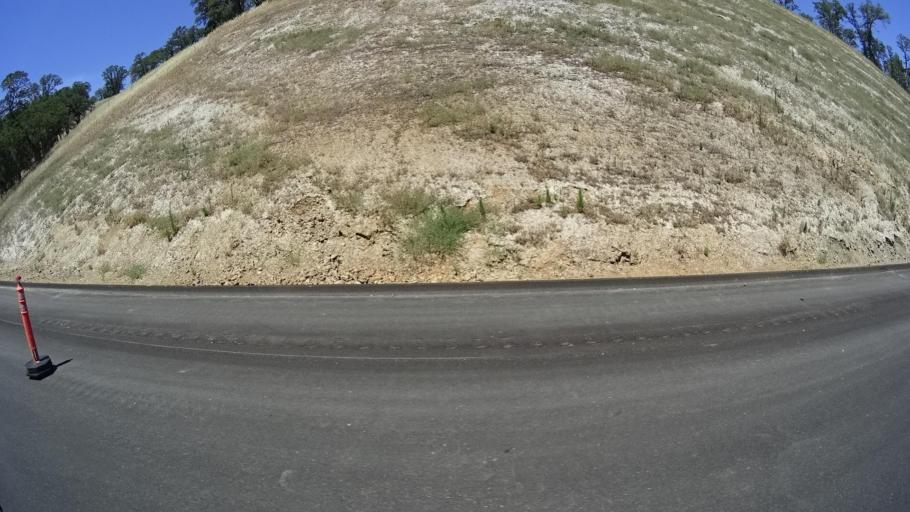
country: US
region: California
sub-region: Lake County
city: Hidden Valley Lake
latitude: 38.8396
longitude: -122.5961
